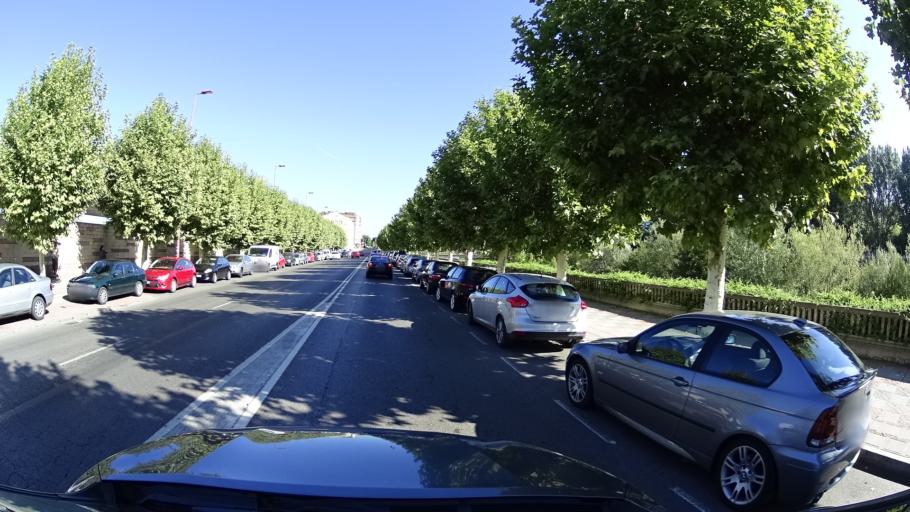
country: ES
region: Castille and Leon
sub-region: Provincia de Leon
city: Leon
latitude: 42.5925
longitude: -5.5782
